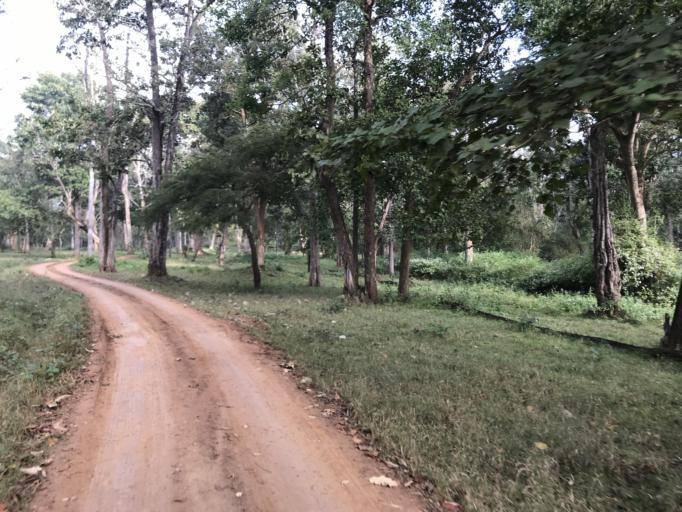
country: IN
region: Karnataka
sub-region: Mysore
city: Heggadadevankote
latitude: 11.9749
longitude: 76.1960
